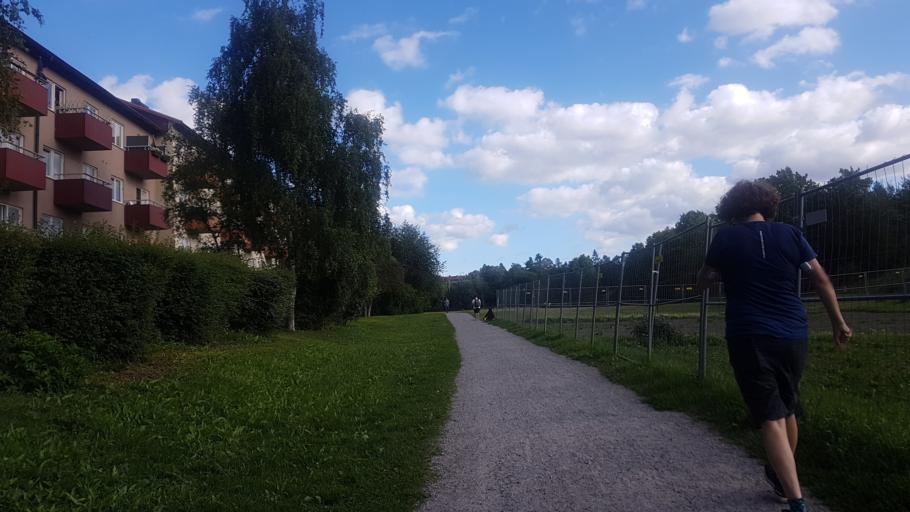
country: SE
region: Stockholm
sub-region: Stockholms Kommun
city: OEstermalm
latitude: 59.2910
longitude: 18.1094
